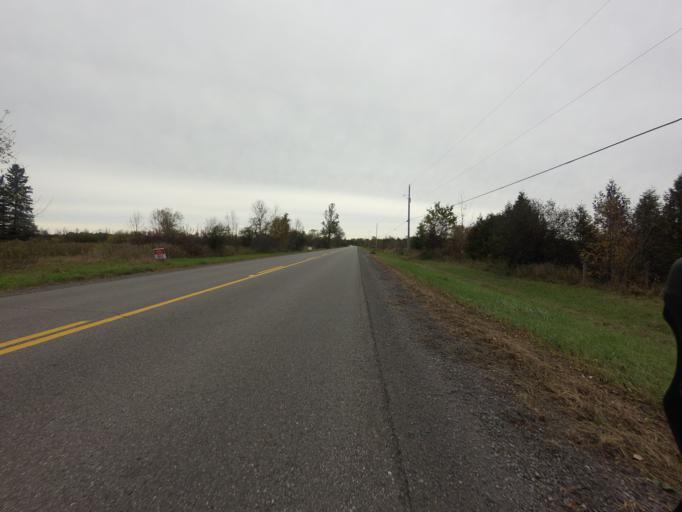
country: CA
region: Ontario
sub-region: Lanark County
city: Smiths Falls
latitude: 44.8605
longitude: -75.8094
